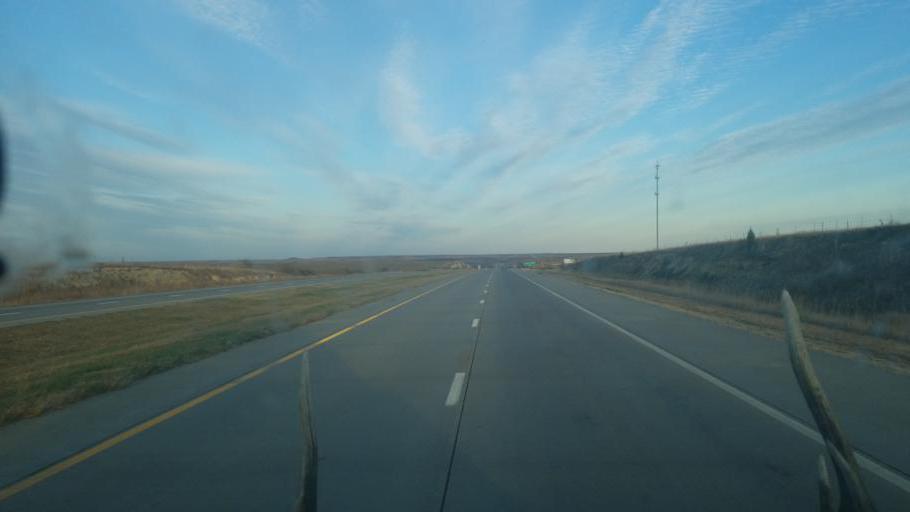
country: US
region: Kansas
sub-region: Riley County
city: Ogden
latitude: 39.0654
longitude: -96.6854
